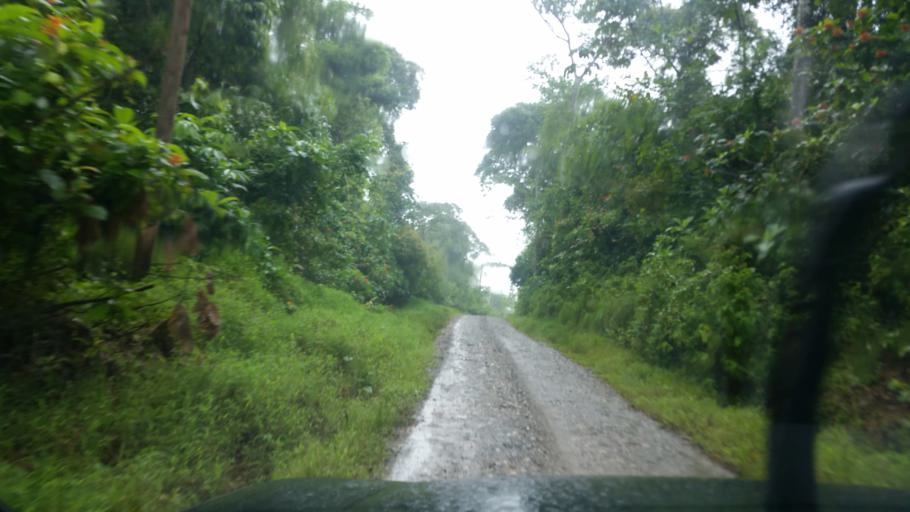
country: NI
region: Atlantico Norte (RAAN)
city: Bonanza
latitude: 14.0757
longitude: -84.6544
